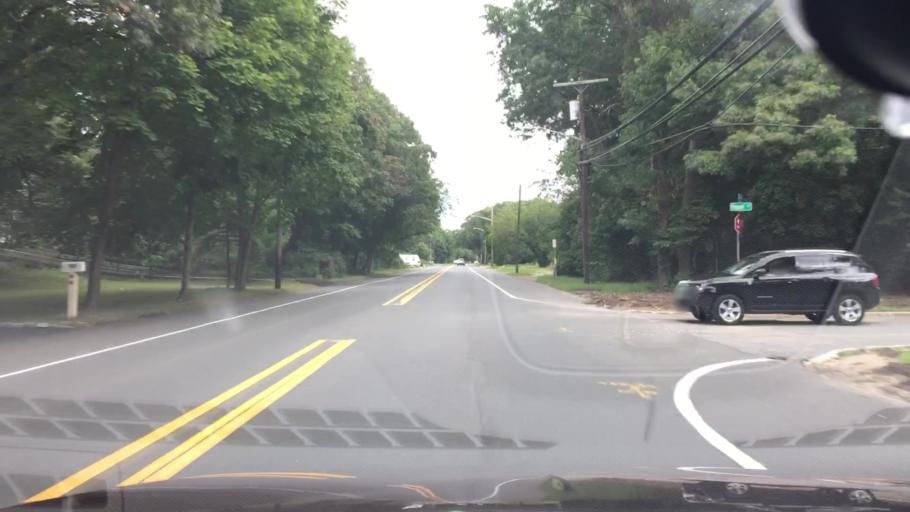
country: US
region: New York
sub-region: Suffolk County
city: Village of the Branch
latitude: 40.8666
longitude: -73.1762
